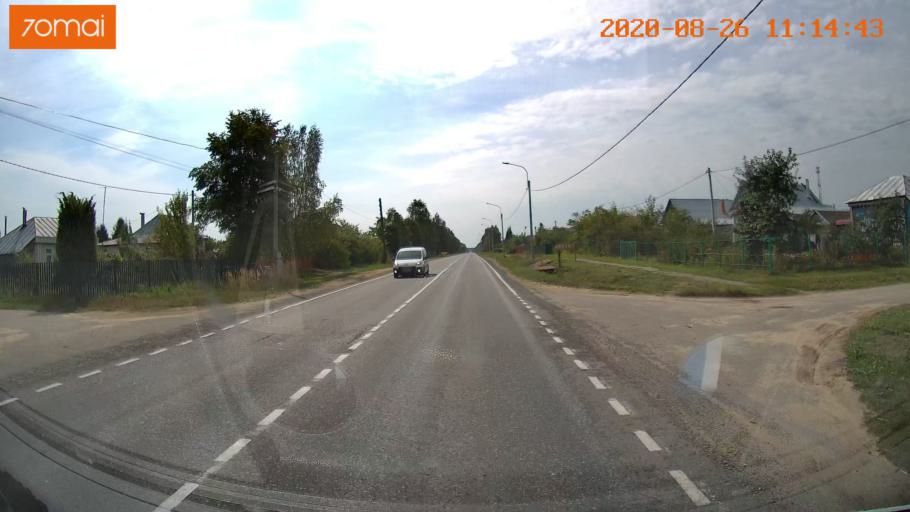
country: RU
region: Rjazan
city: Izhevskoye
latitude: 54.4462
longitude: 41.1162
